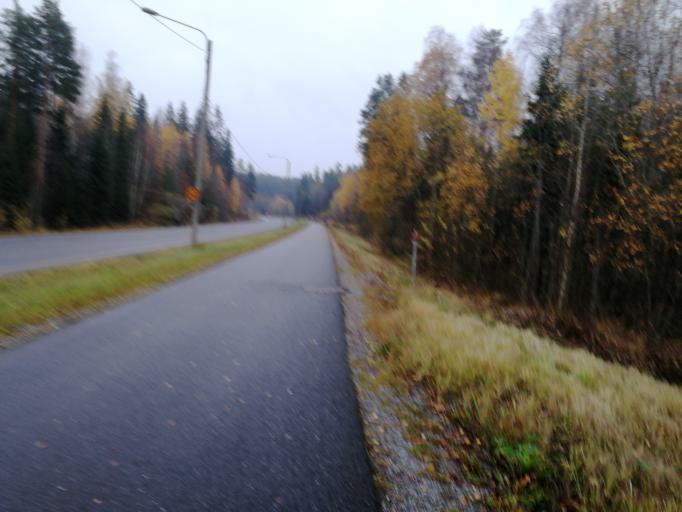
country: FI
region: Pirkanmaa
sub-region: Tampere
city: Tampere
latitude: 61.4490
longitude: 23.8717
